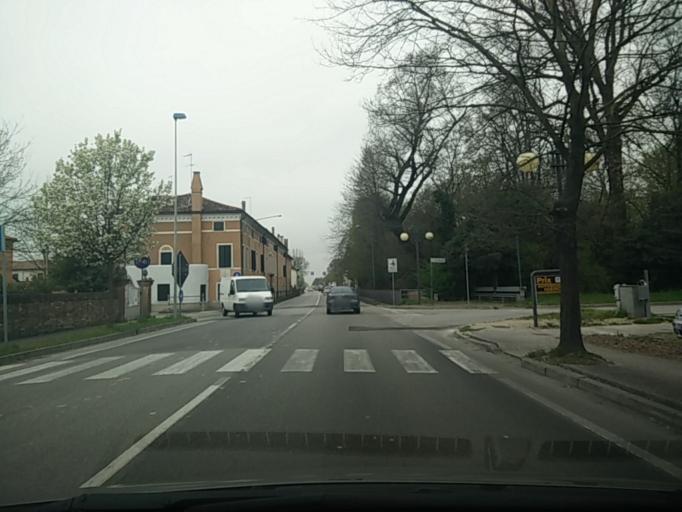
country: IT
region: Veneto
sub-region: Provincia di Venezia
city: Mirano
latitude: 45.4926
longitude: 12.0999
